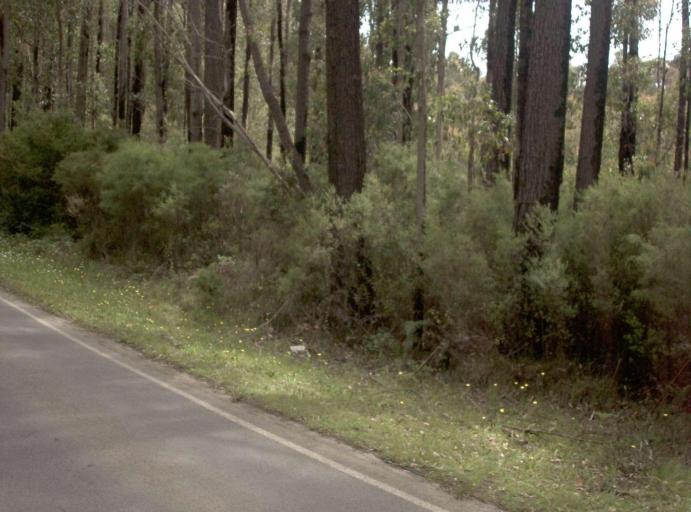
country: AU
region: Victoria
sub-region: Latrobe
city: Traralgon
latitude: -38.0037
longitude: 146.4140
